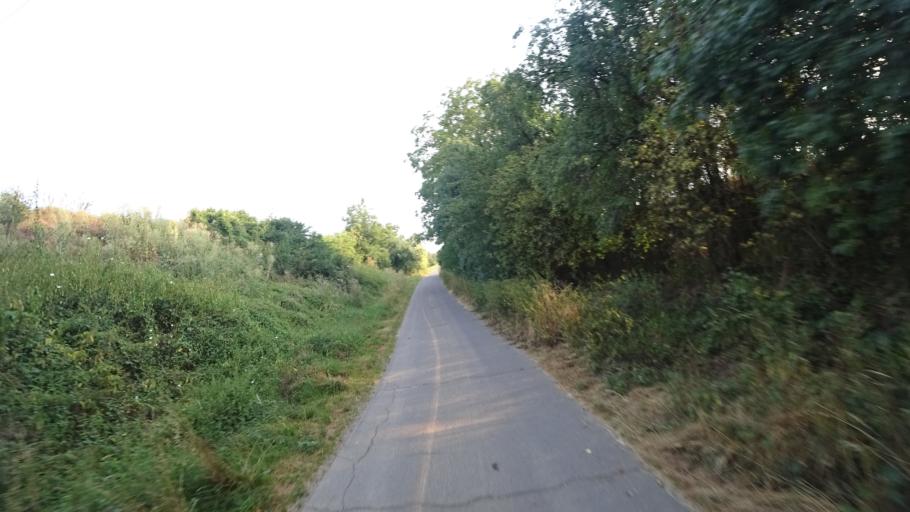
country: DE
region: Rheinland-Pfalz
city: Weitersburg
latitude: 50.4180
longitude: 7.6125
